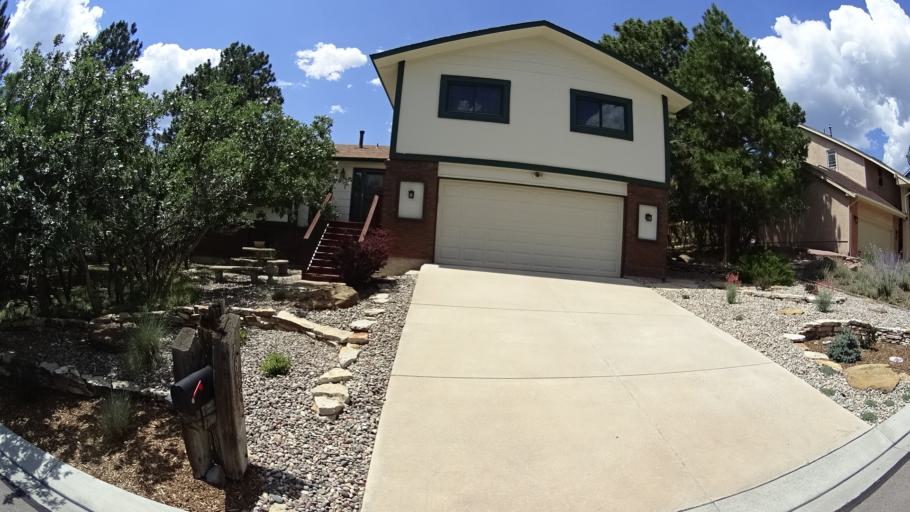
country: US
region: Colorado
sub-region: El Paso County
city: Air Force Academy
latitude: 38.9382
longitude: -104.8469
